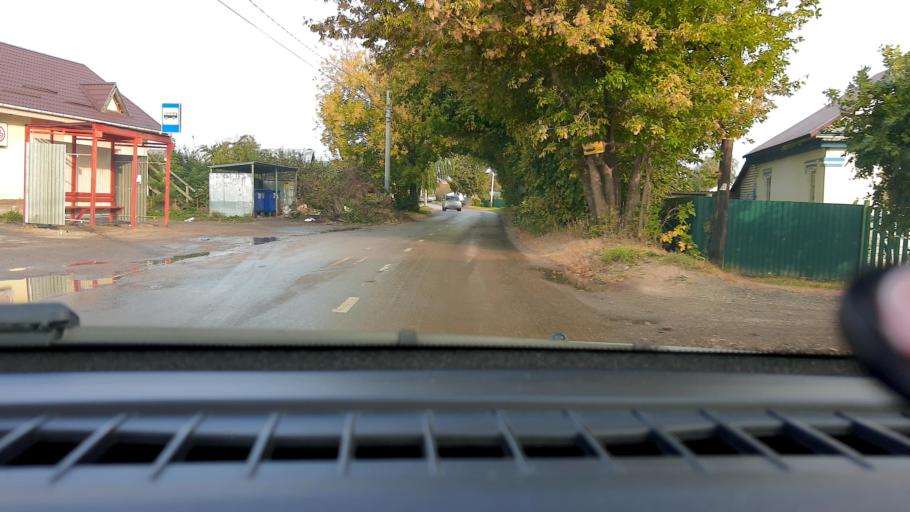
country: RU
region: Nizjnij Novgorod
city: Kstovo
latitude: 56.1897
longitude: 44.1616
